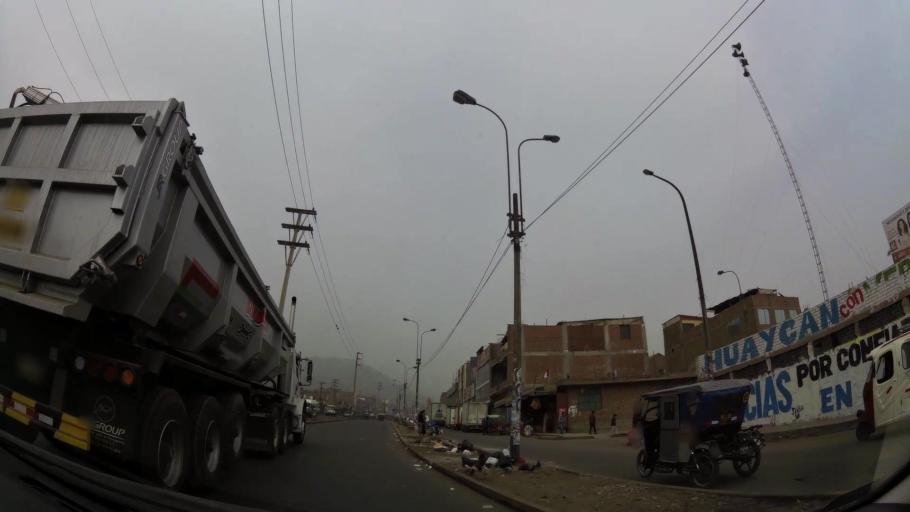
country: PE
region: Lima
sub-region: Lima
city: Chaclacayo
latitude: -12.0081
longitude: -76.8248
